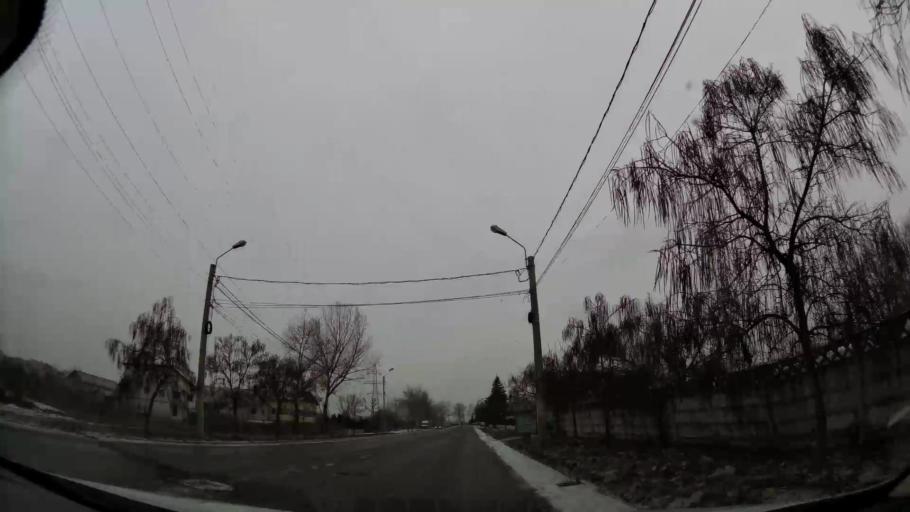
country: RO
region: Dambovita
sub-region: Municipiul Targoviste
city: Targoviste
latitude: 44.9302
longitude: 25.4769
